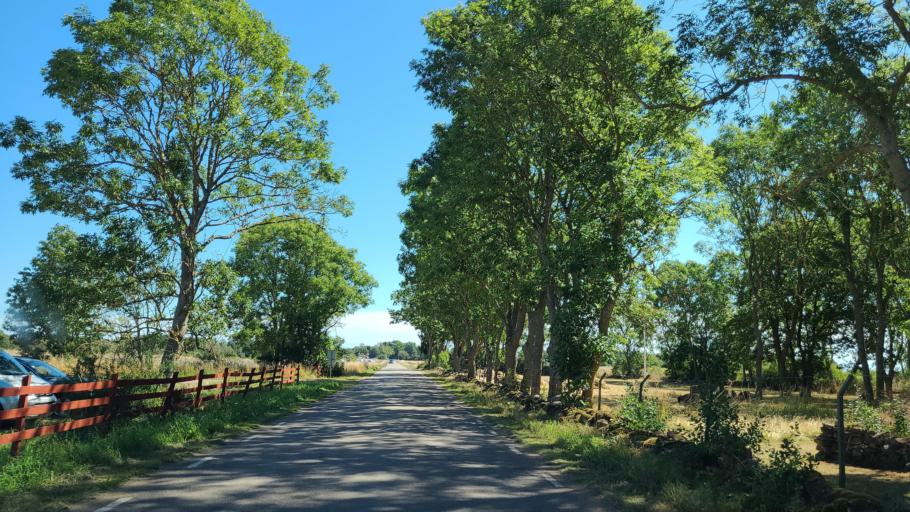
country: SE
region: Kalmar
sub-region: Borgholms Kommun
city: Borgholm
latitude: 56.7401
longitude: 16.7115
